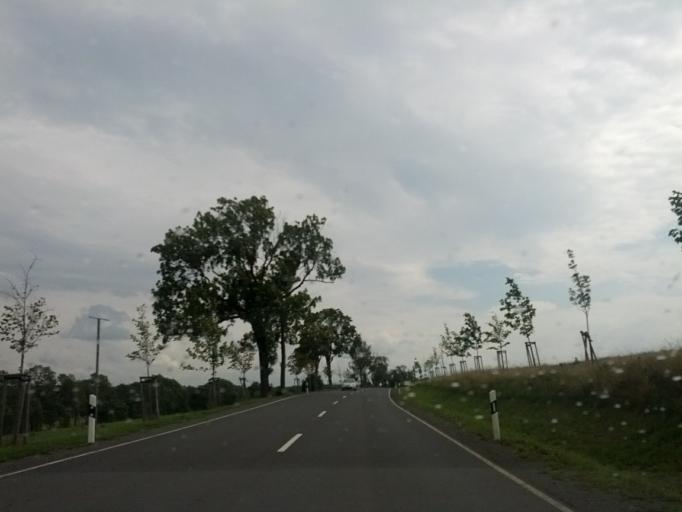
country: DE
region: Thuringia
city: Ernstroda
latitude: 50.8557
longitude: 10.6463
